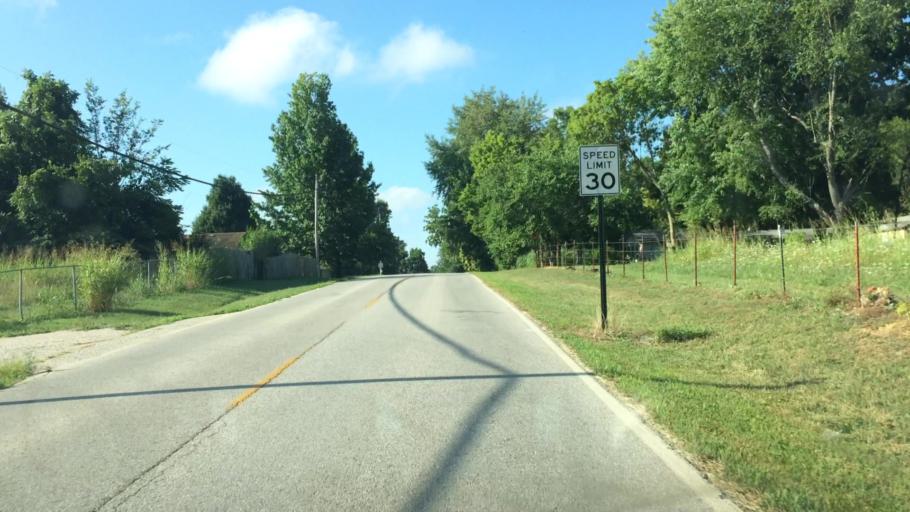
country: US
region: Missouri
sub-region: Greene County
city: Springfield
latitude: 37.2616
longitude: -93.2808
